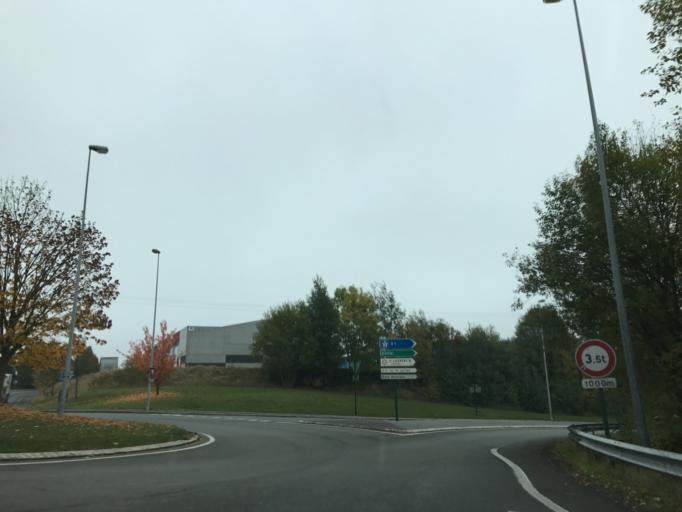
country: FR
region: Nord-Pas-de-Calais
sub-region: Departement du Pas-de-Calais
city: Saint-Laurent-Blangy
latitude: 50.3091
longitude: 2.8020
